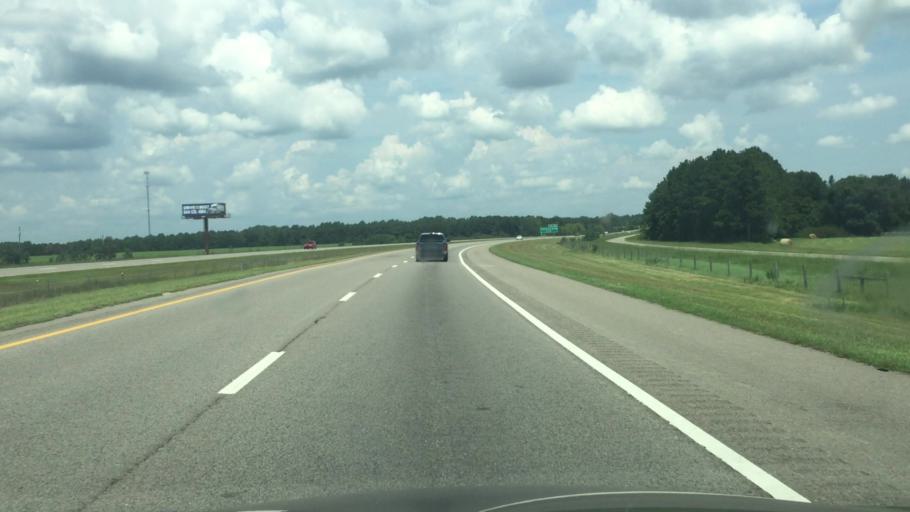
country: US
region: North Carolina
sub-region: Richmond County
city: Ellerbe
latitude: 35.1916
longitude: -79.7257
